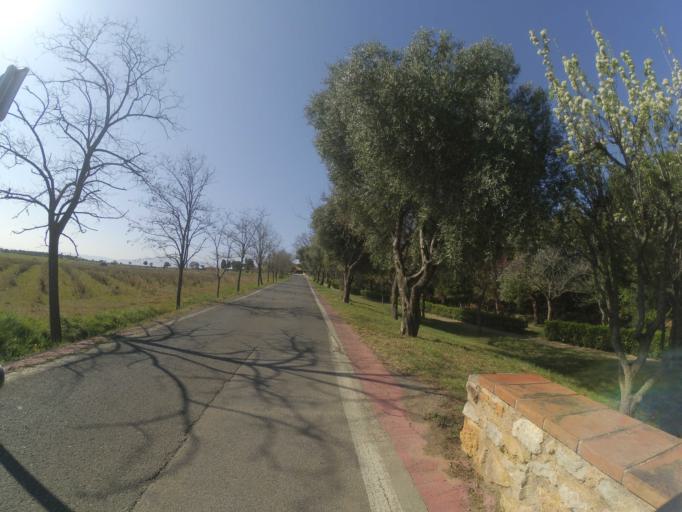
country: FR
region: Languedoc-Roussillon
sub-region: Departement des Pyrenees-Orientales
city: Thuir
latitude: 42.6170
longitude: 2.7490
